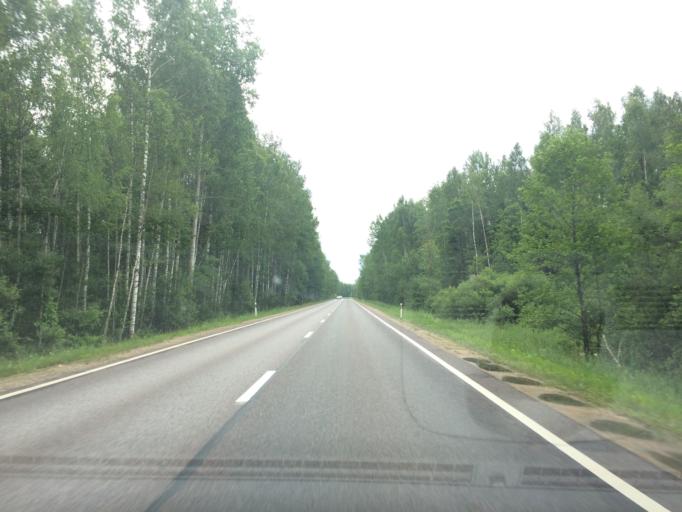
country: LV
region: Livani
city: Livani
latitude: 56.5407
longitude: 26.1274
